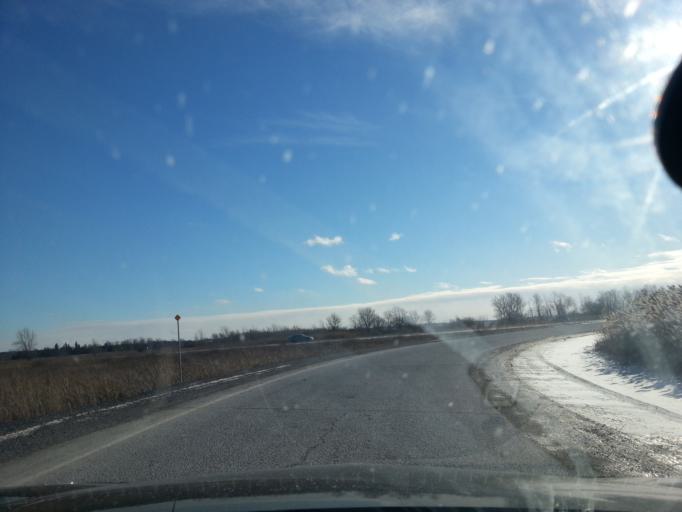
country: CA
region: Ontario
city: Casselman
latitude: 45.3274
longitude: -74.9836
